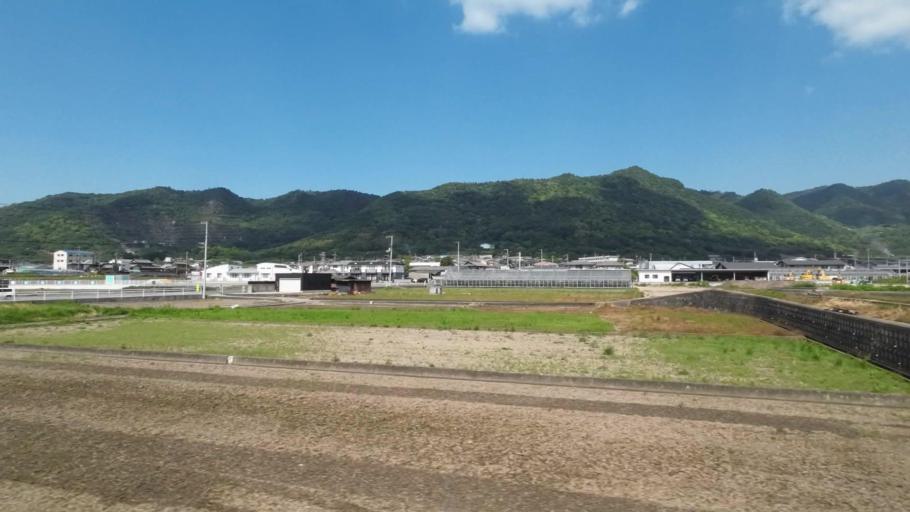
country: JP
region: Kagawa
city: Kan'onjicho
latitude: 34.1519
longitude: 133.6874
